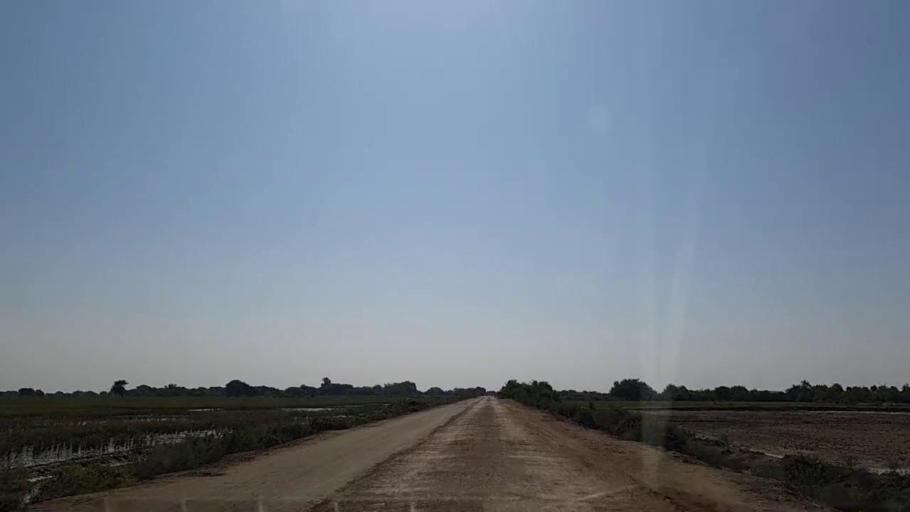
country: PK
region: Sindh
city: Chuhar Jamali
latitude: 24.5188
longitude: 68.0942
